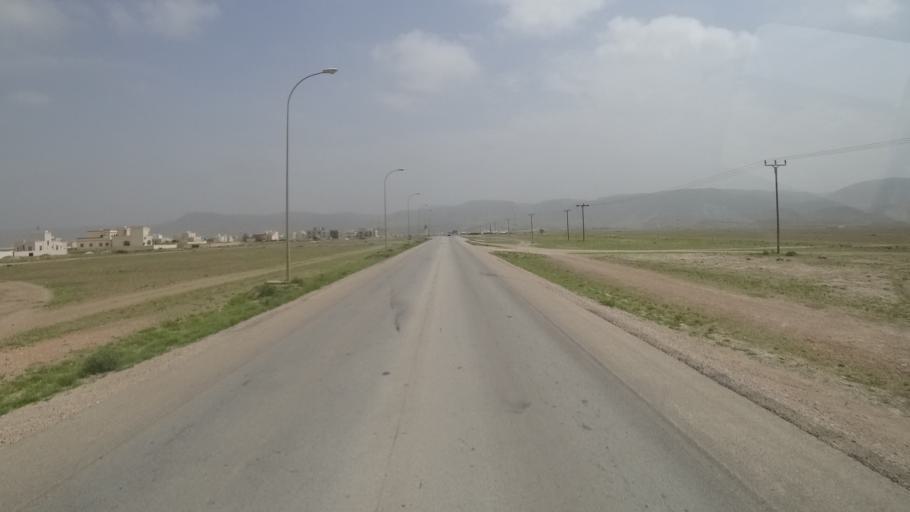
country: OM
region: Zufar
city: Salalah
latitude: 17.0935
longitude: 54.2169
